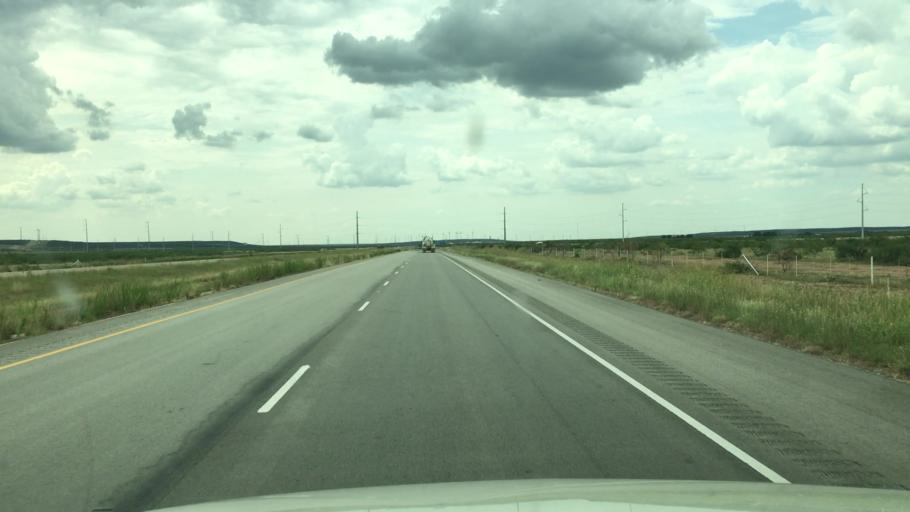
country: US
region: Texas
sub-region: Sterling County
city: Sterling City
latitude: 31.9585
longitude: -101.2053
